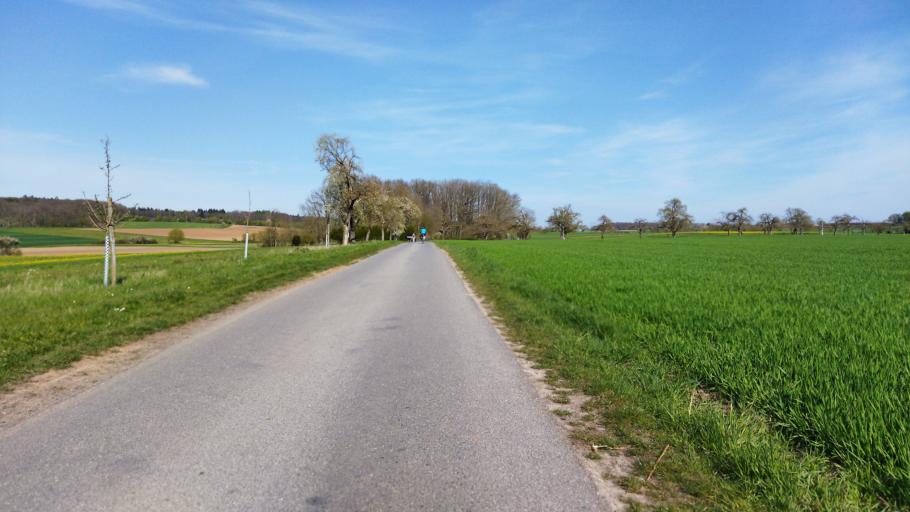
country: DE
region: Baden-Wuerttemberg
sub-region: Regierungsbezirk Stuttgart
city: Freudental
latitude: 48.9848
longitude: 9.0603
